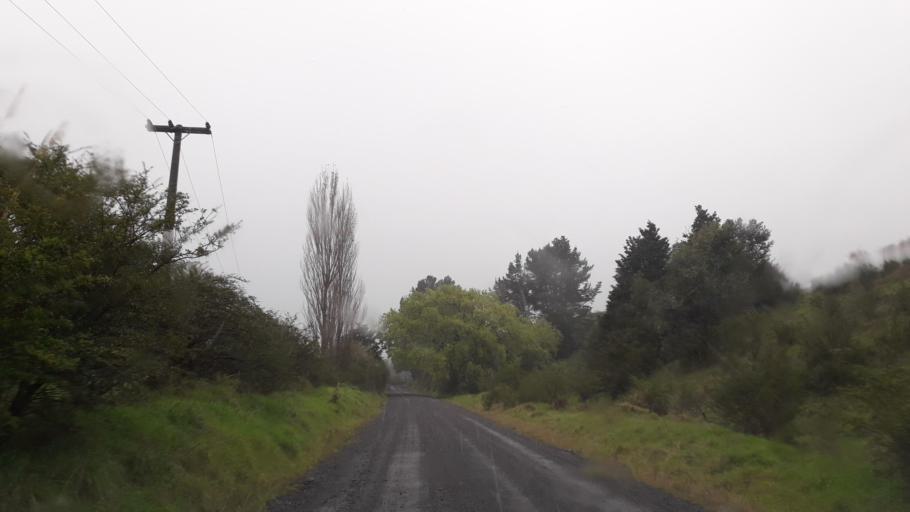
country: NZ
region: Northland
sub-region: Far North District
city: Waimate North
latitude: -35.4867
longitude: 173.7009
